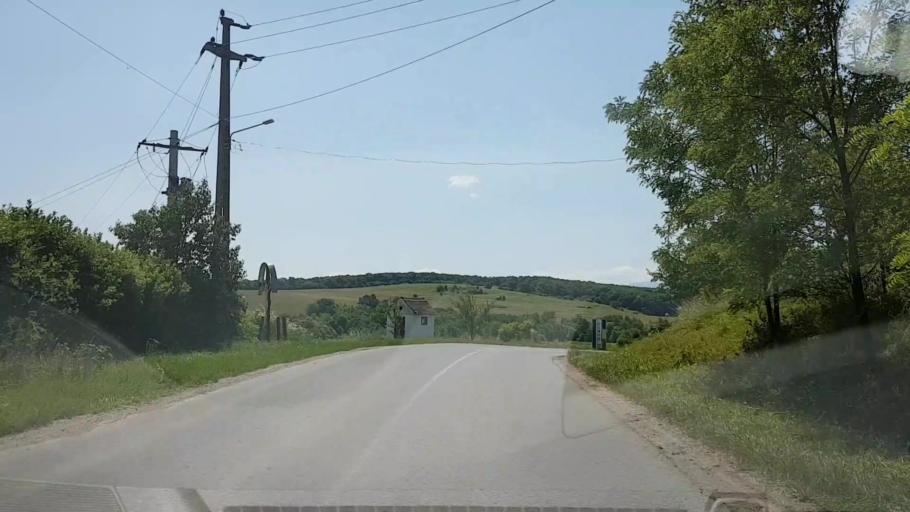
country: RO
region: Brasov
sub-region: Comuna Cincu
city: Cincu
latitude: 45.9076
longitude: 24.8112
